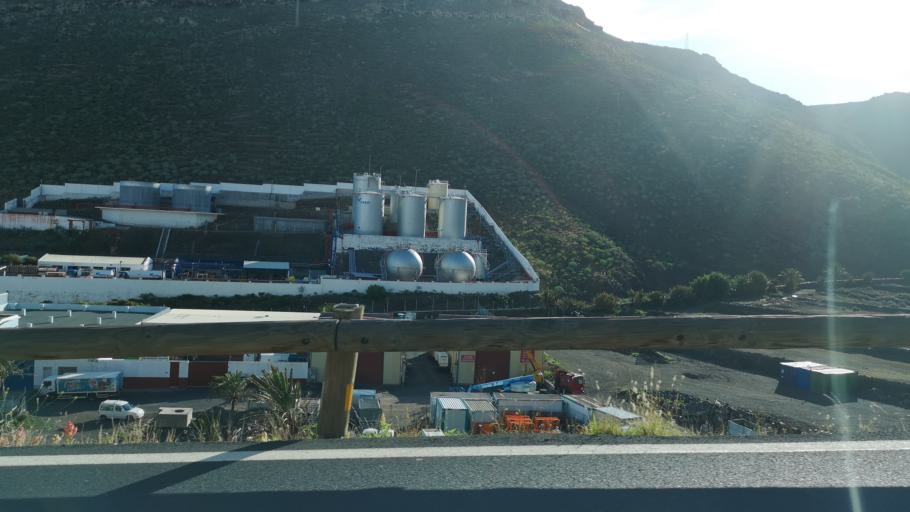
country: ES
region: Canary Islands
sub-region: Provincia de Santa Cruz de Tenerife
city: San Sebastian de la Gomera
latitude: 28.0898
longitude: -17.1177
